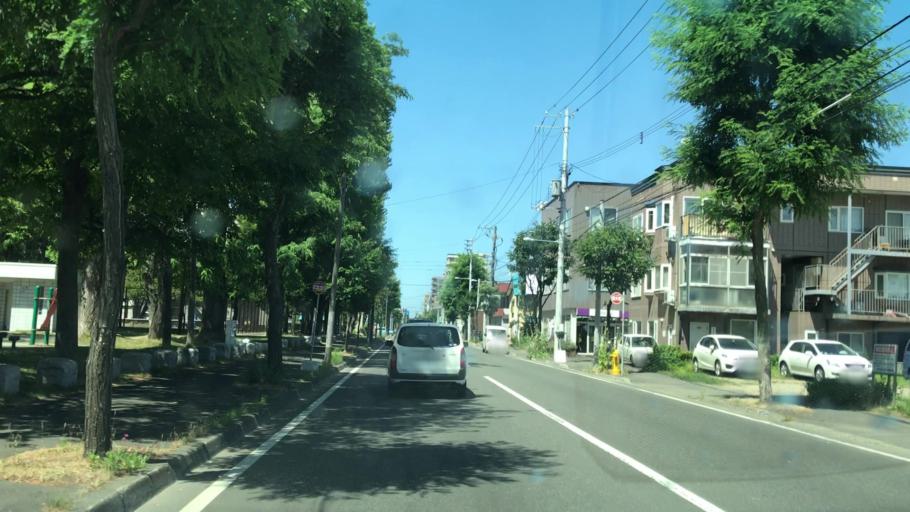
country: JP
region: Hokkaido
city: Sapporo
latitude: 43.0527
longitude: 141.3954
